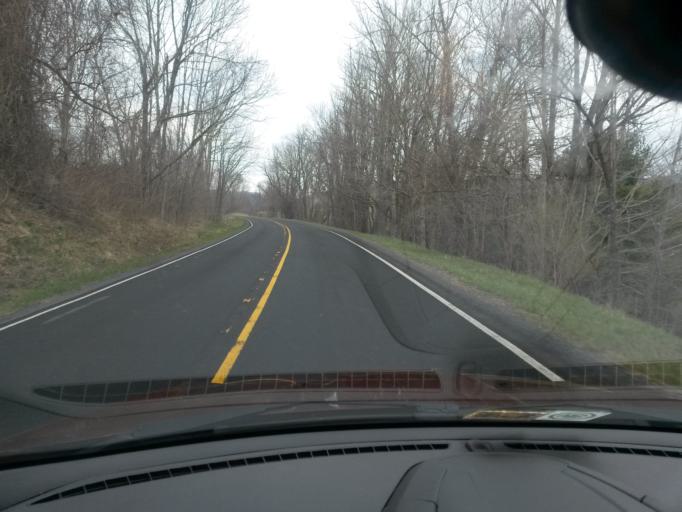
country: US
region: Virginia
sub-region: Bath County
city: Warm Springs
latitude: 38.0624
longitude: -79.7750
